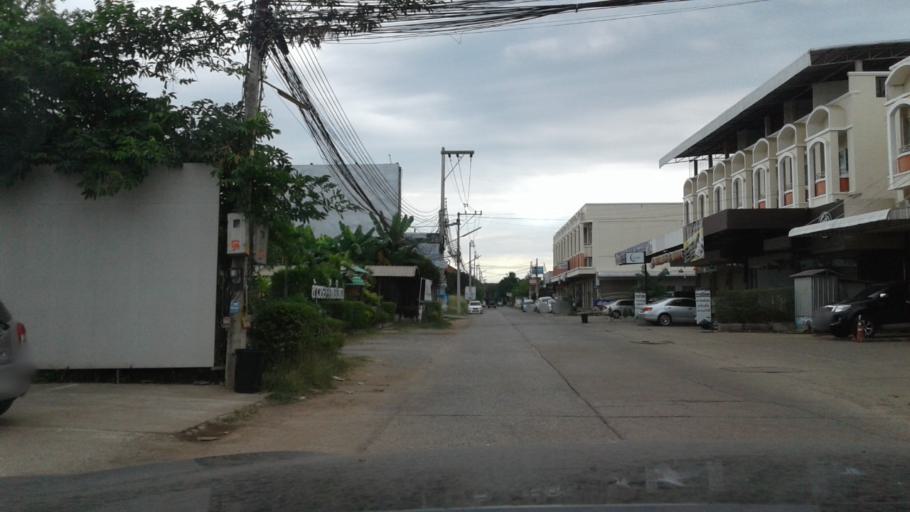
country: TH
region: Changwat Udon Thani
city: Udon Thani
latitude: 17.3999
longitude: 102.7734
